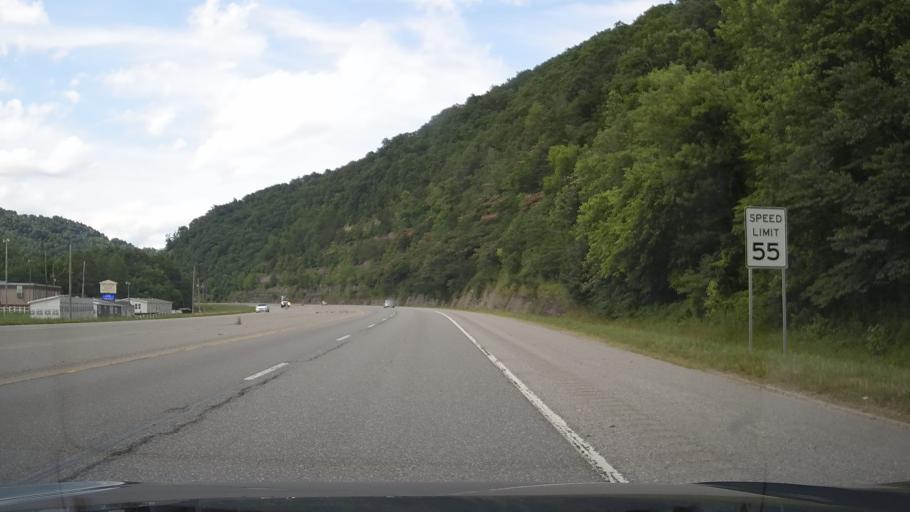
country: US
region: Kentucky
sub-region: Pike County
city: Coal Run Village
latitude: 37.5839
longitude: -82.6597
